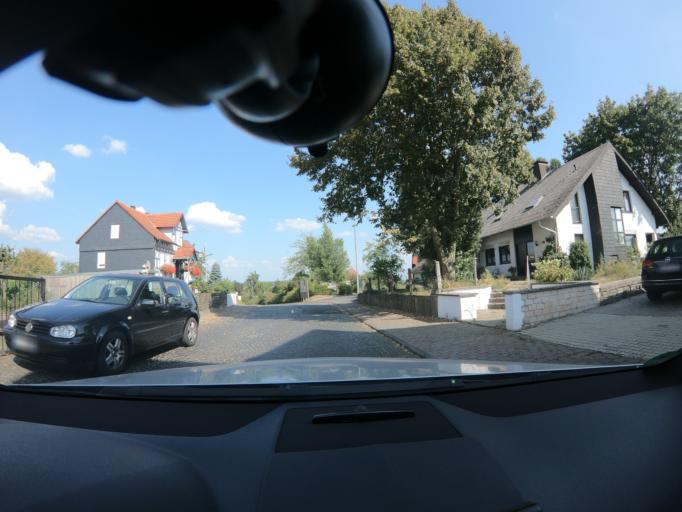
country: DE
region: Hesse
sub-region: Regierungsbezirk Giessen
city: Rauschenberg
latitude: 50.8733
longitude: 8.9531
